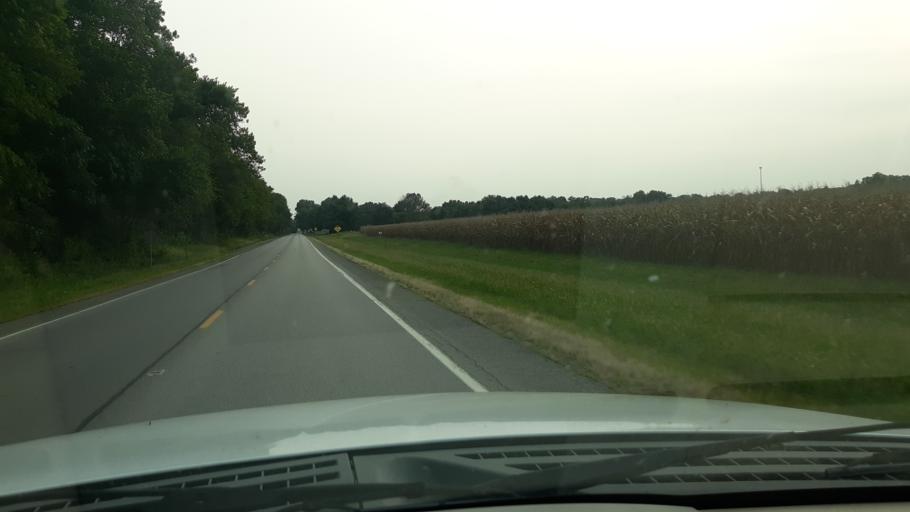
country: US
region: Illinois
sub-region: Edwards County
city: Grayville
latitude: 38.1704
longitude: -88.0572
